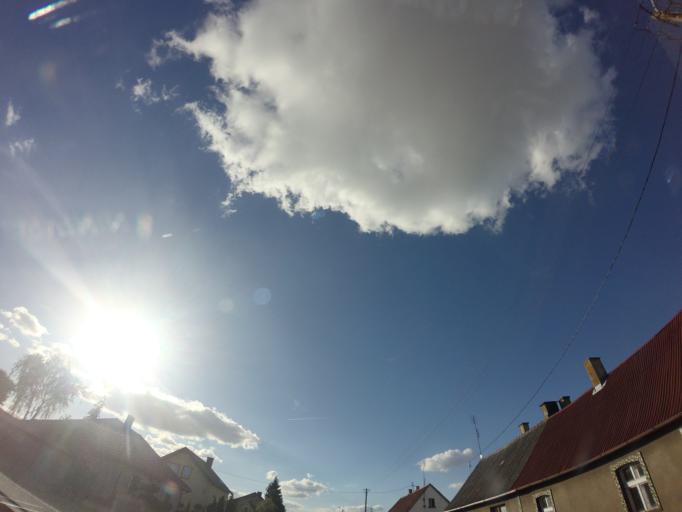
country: PL
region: Greater Poland Voivodeship
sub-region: Powiat grodziski
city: Wielichowo
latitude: 52.0670
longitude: 16.4040
